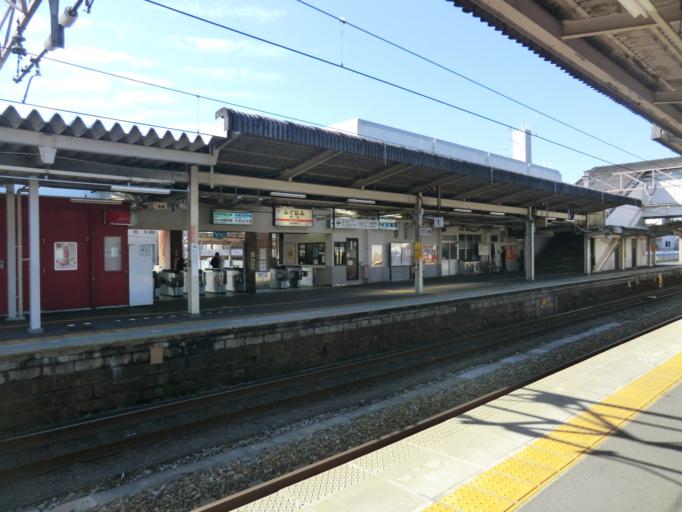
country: JP
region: Gifu
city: Mizunami
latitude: 35.3690
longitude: 137.2526
